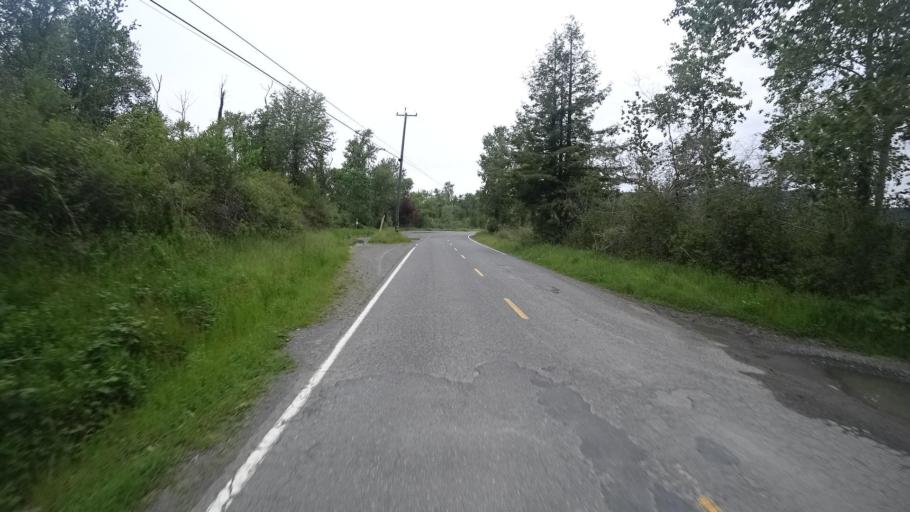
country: US
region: California
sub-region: Humboldt County
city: Blue Lake
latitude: 40.8729
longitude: -123.9935
